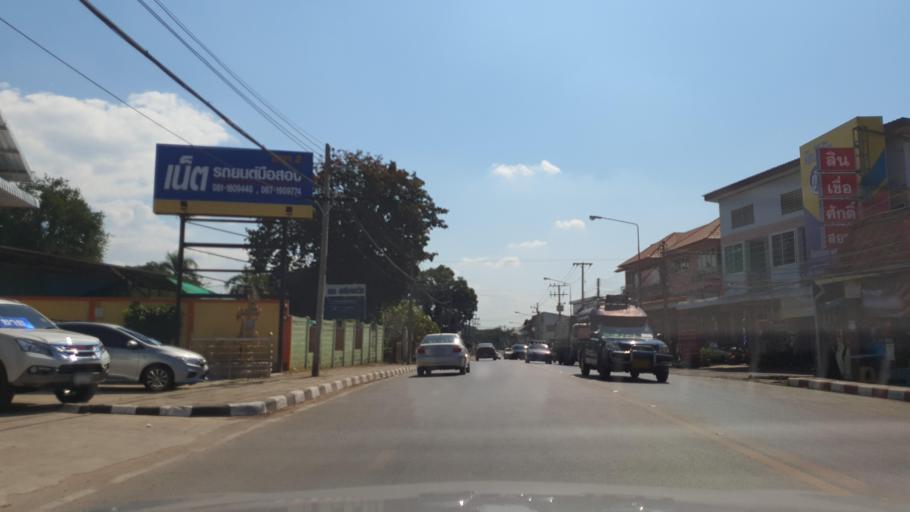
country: TH
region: Nan
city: Nan
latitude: 18.7953
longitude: 100.7794
